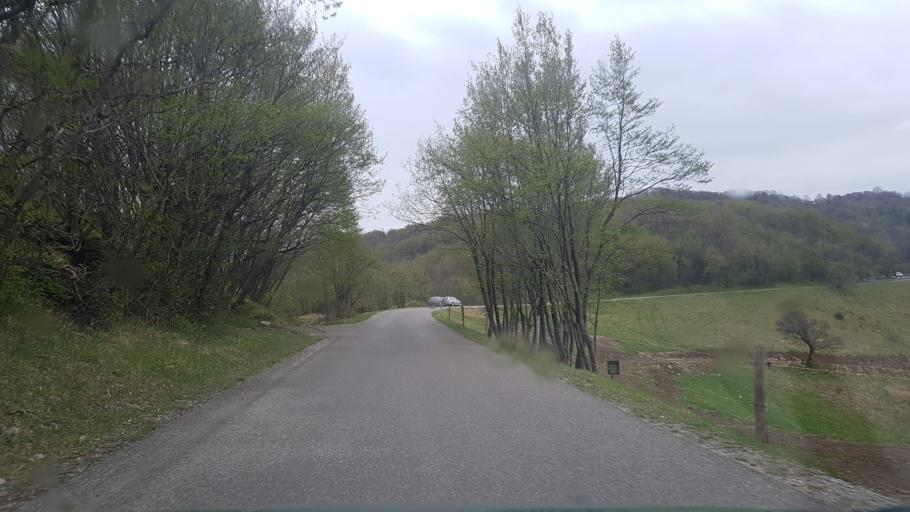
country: SI
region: Kanal
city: Deskle
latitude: 46.0383
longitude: 13.5670
